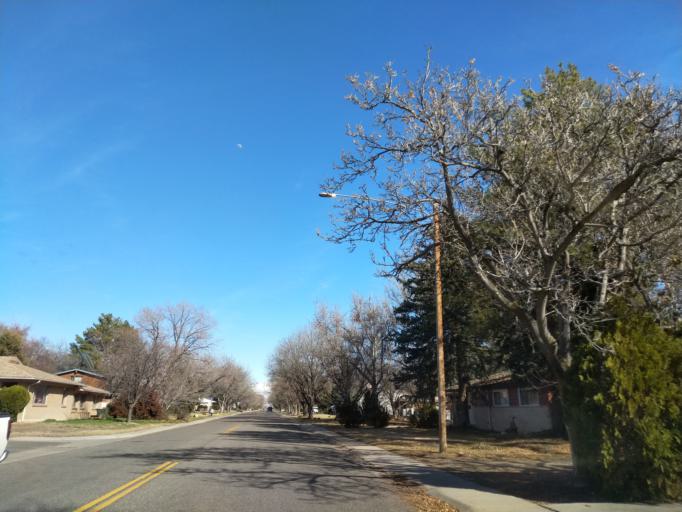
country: US
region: Colorado
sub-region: Mesa County
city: Grand Junction
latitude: 39.0846
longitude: -108.5670
